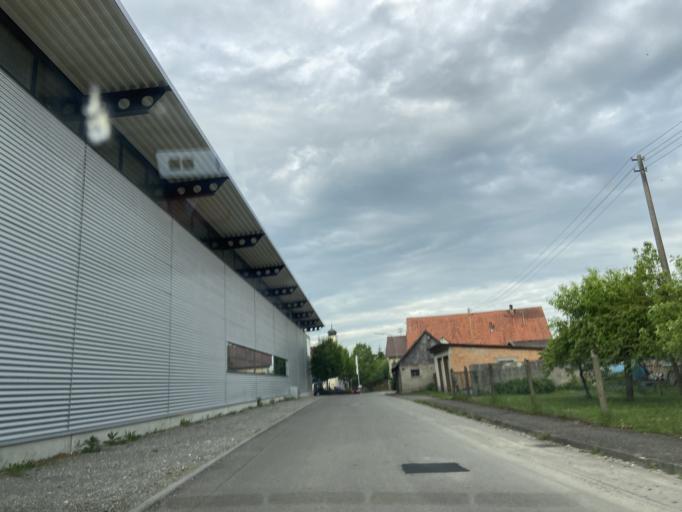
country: DE
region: Baden-Wuerttemberg
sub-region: Tuebingen Region
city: Hohentengen
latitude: 48.0343
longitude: 9.3736
